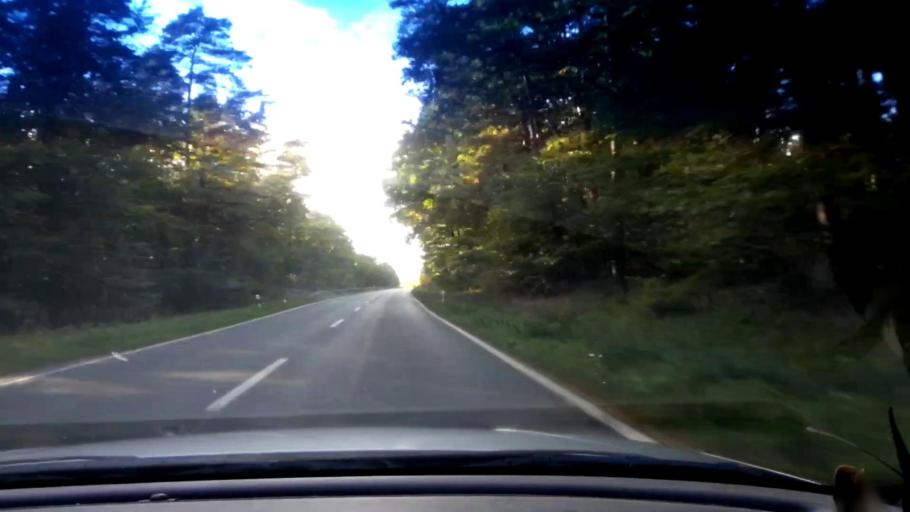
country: DE
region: Bavaria
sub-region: Upper Franconia
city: Strullendorf
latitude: 49.8573
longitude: 10.9816
